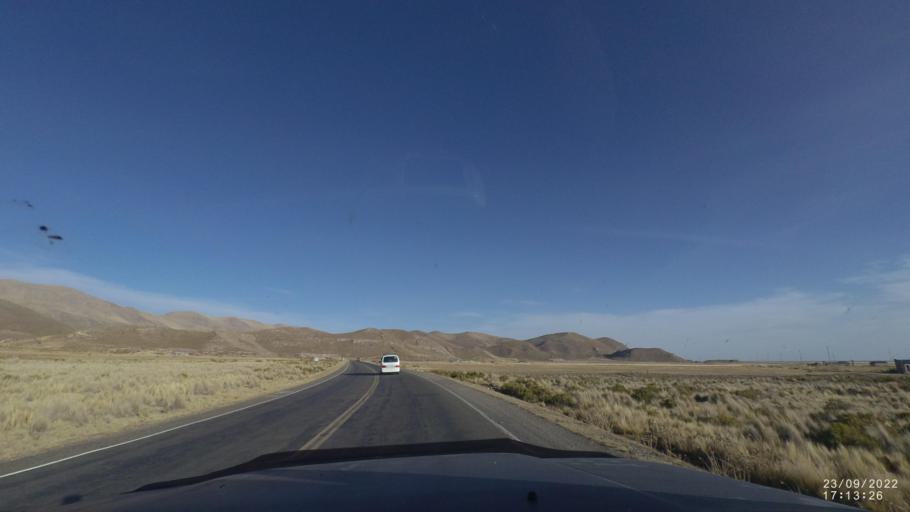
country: BO
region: Oruro
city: Totoral
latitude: -18.7109
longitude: -66.8746
